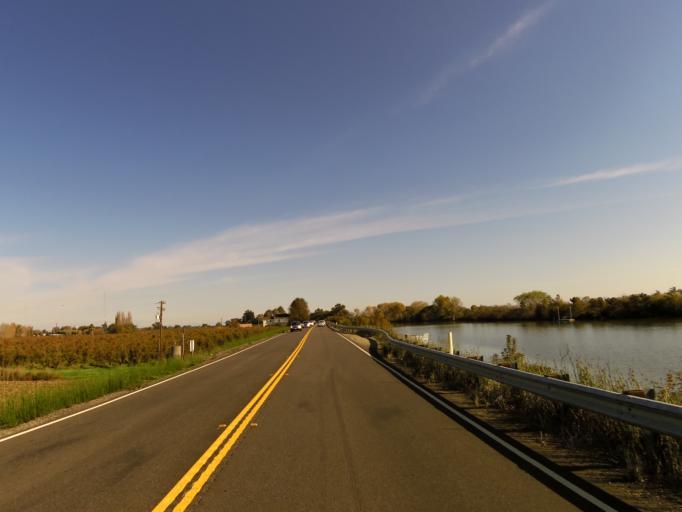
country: US
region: California
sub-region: Sacramento County
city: Walnut Grove
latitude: 38.1926
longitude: -121.5705
